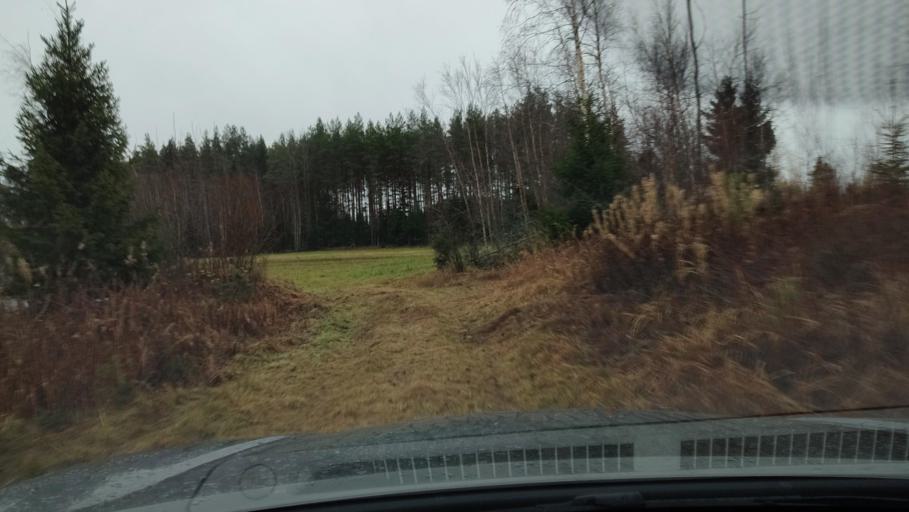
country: FI
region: Southern Ostrobothnia
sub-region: Suupohja
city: Karijoki
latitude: 62.2227
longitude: 21.5525
